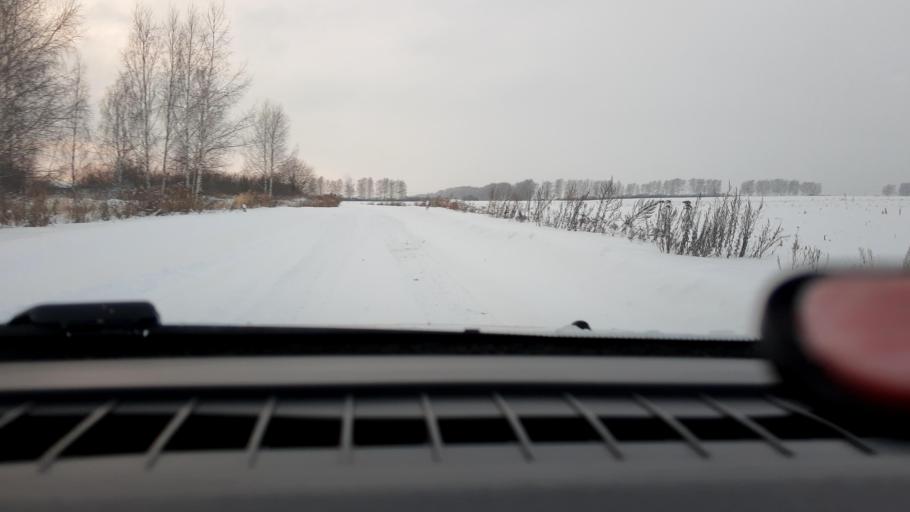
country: RU
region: Nizjnij Novgorod
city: Burevestnik
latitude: 56.1306
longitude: 43.9597
